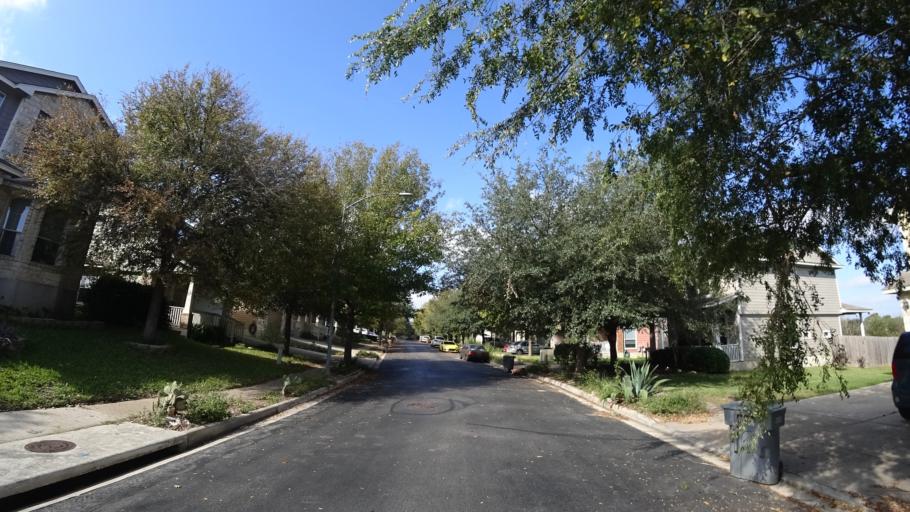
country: US
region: Texas
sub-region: Travis County
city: Manchaca
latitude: 30.1891
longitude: -97.8155
